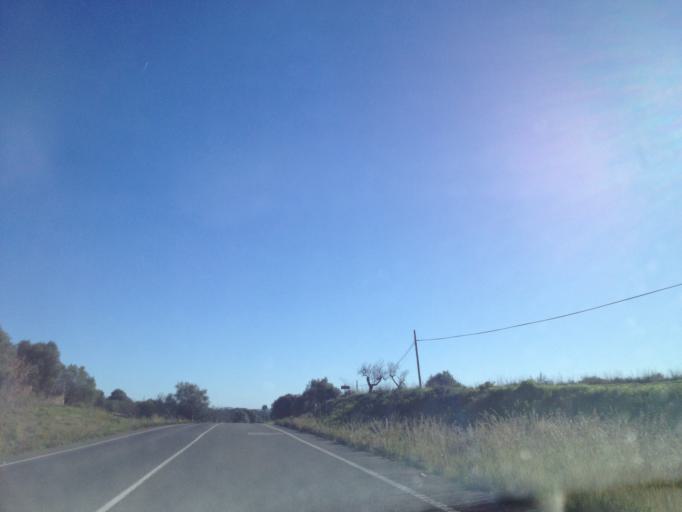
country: ES
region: Balearic Islands
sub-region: Illes Balears
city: Sineu
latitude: 39.6445
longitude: 3.0405
